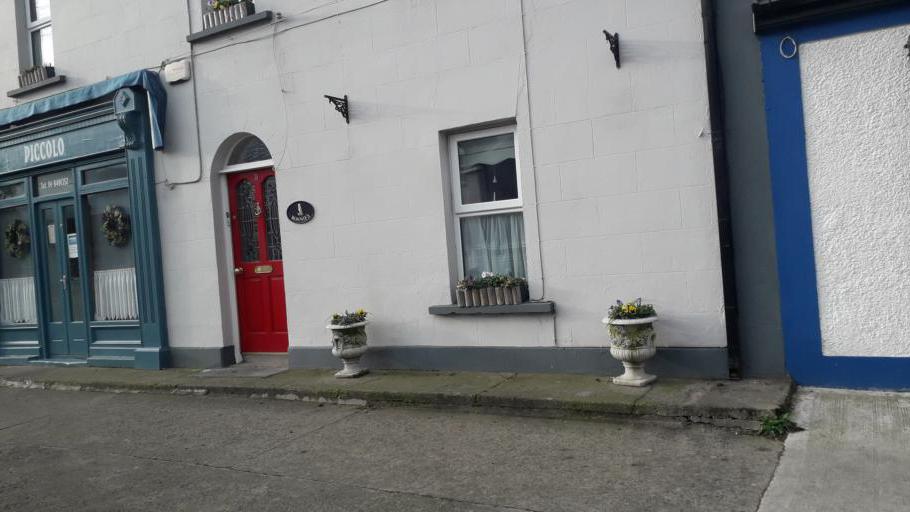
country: IE
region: Leinster
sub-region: Fingal County
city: Skerries
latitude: 53.5789
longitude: -6.1110
